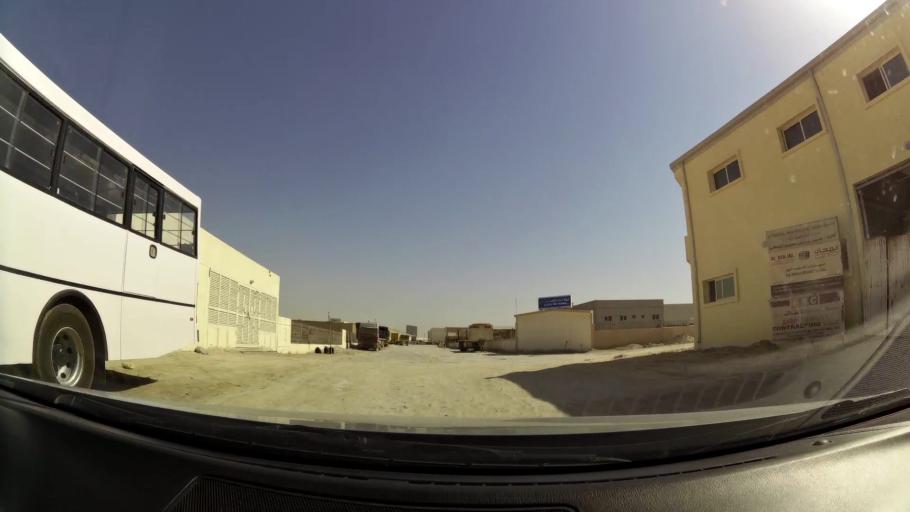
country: AE
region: Dubai
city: Dubai
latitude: 25.0059
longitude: 55.1183
